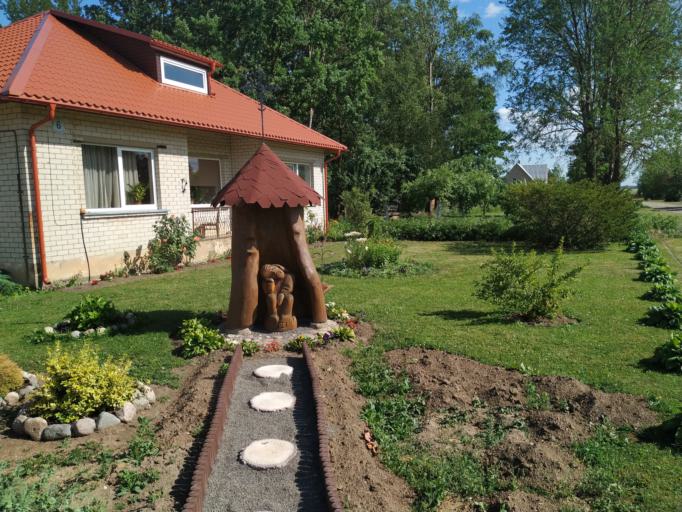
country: LT
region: Panevezys
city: Pasvalys
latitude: 56.1135
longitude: 24.3509
